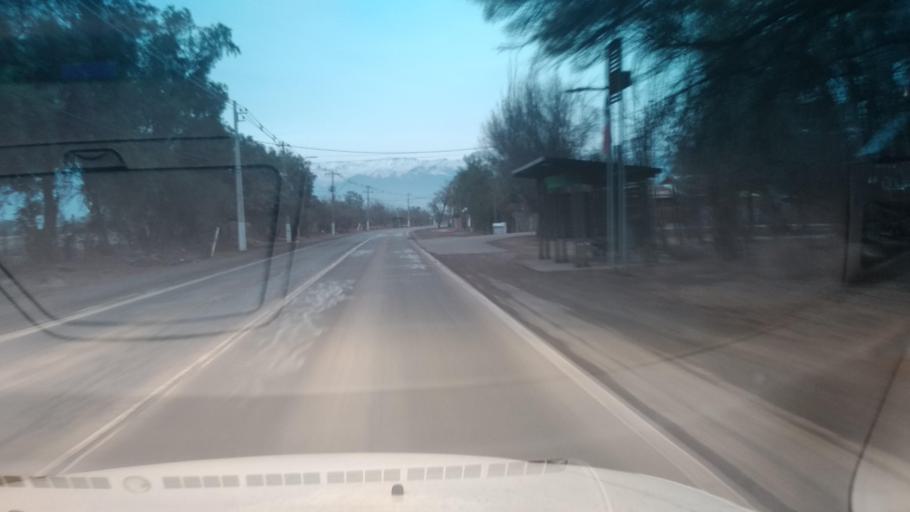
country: CL
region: Santiago Metropolitan
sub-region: Provincia de Chacabuco
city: Chicureo Abajo
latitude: -33.0923
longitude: -70.7291
